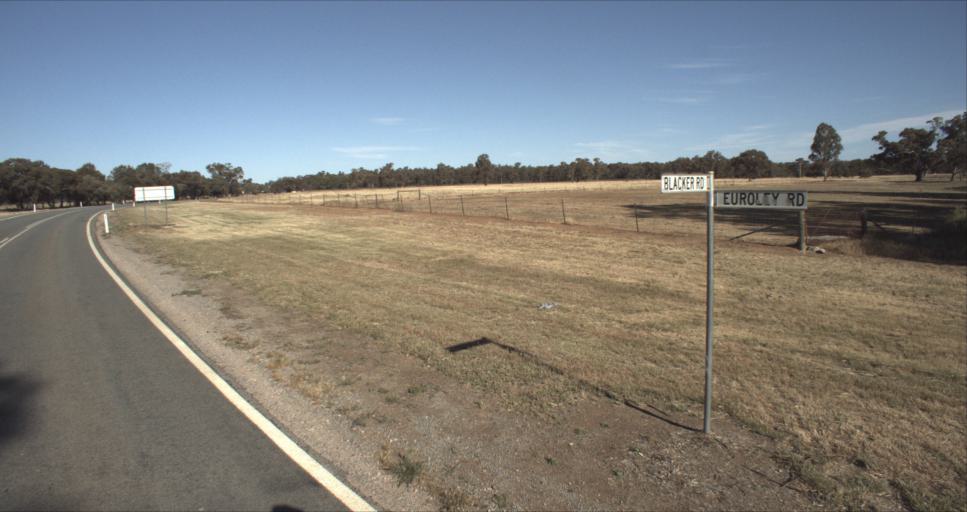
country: AU
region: New South Wales
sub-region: Leeton
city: Leeton
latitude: -34.6234
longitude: 146.3840
